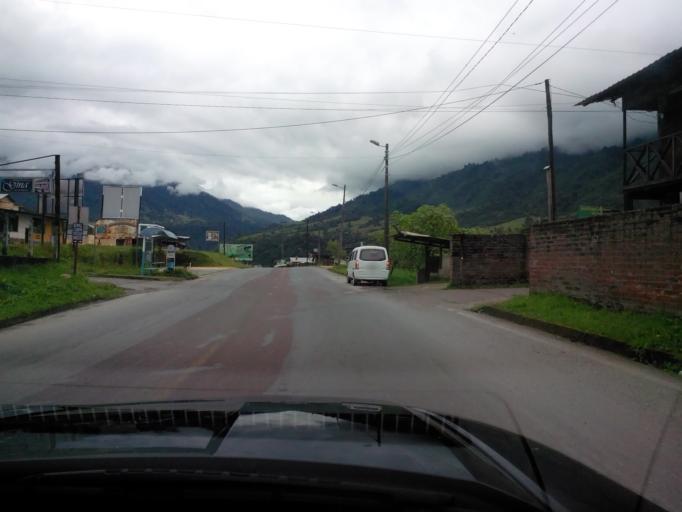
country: EC
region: Napo
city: Archidona
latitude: -0.4622
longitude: -77.8940
